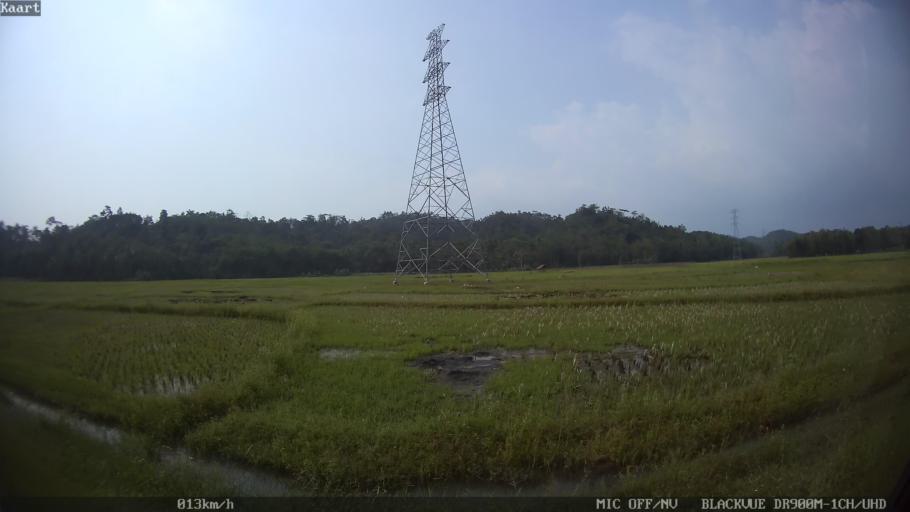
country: ID
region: Lampung
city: Gadingrejo
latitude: -5.4076
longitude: 105.0185
